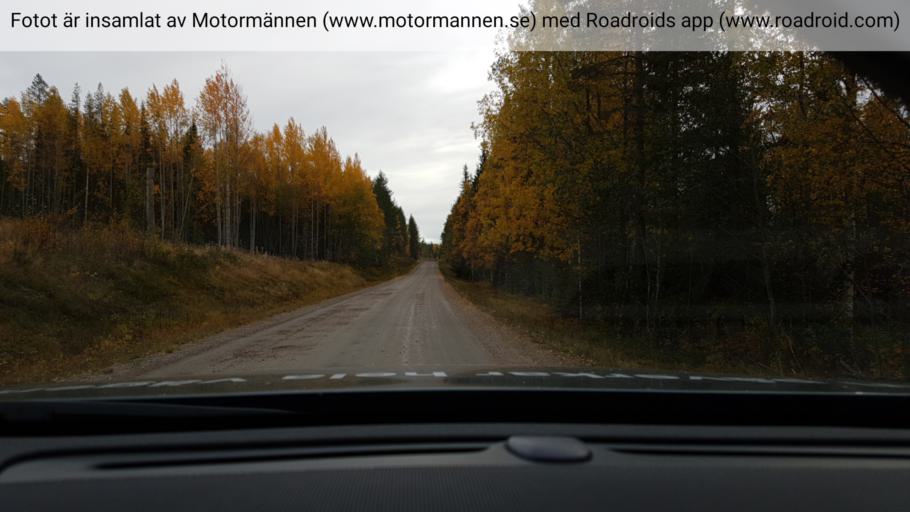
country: SE
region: Norrbotten
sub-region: Overkalix Kommun
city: OEverkalix
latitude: 66.2869
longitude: 22.9732
